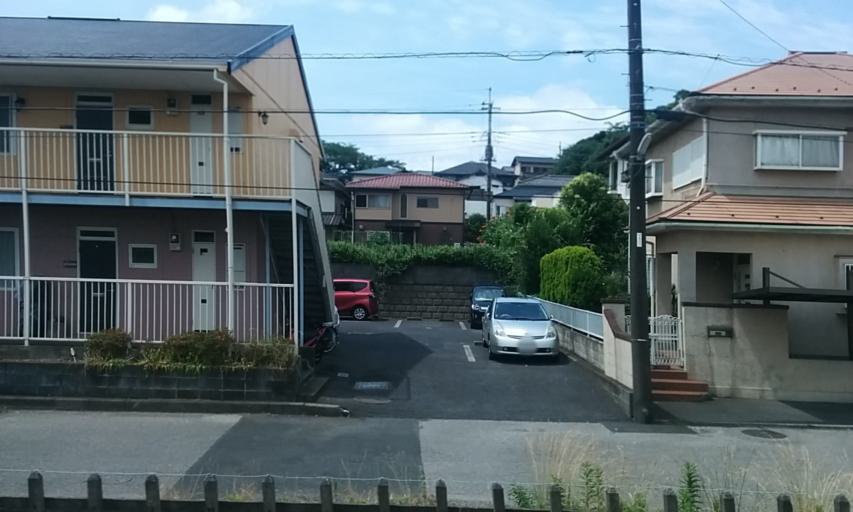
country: JP
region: Chiba
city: Sakura
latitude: 35.7382
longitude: 140.2037
